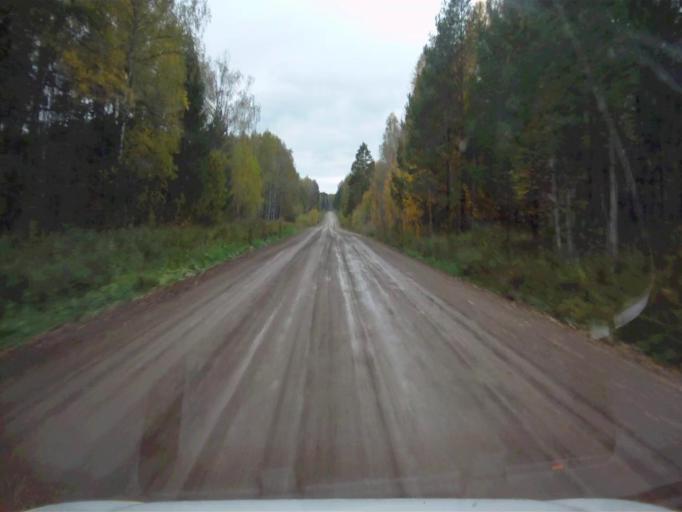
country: RU
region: Chelyabinsk
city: Nyazepetrovsk
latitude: 56.0927
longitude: 59.4092
